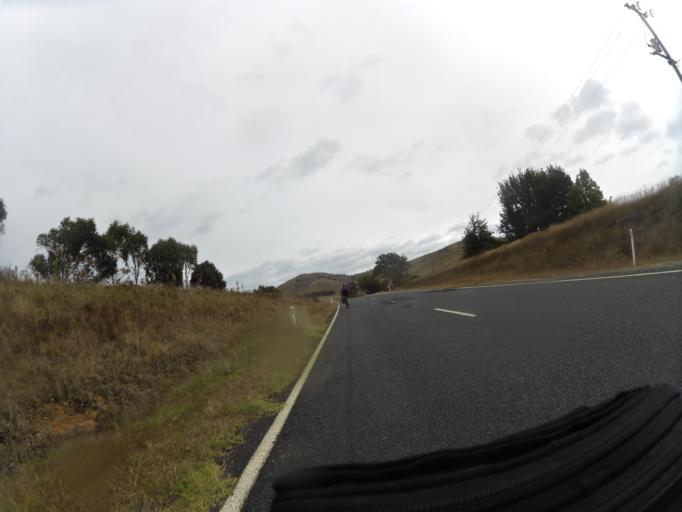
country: AU
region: New South Wales
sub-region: Greater Hume Shire
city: Holbrook
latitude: -36.2034
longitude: 147.7459
